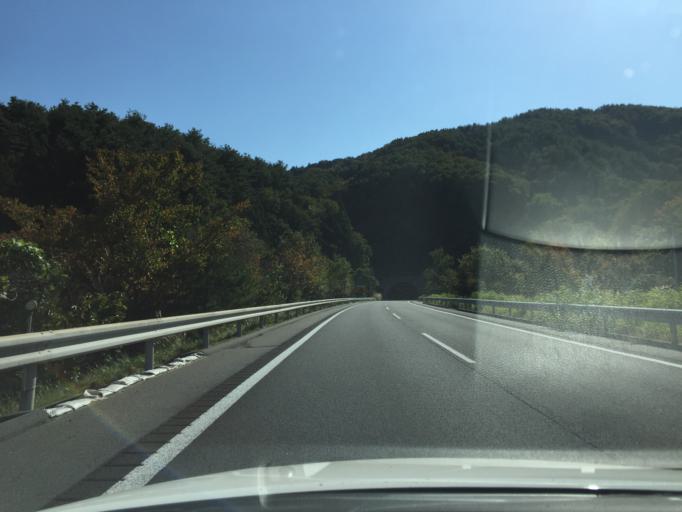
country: JP
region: Fukushima
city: Iwaki
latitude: 37.1293
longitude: 140.7541
